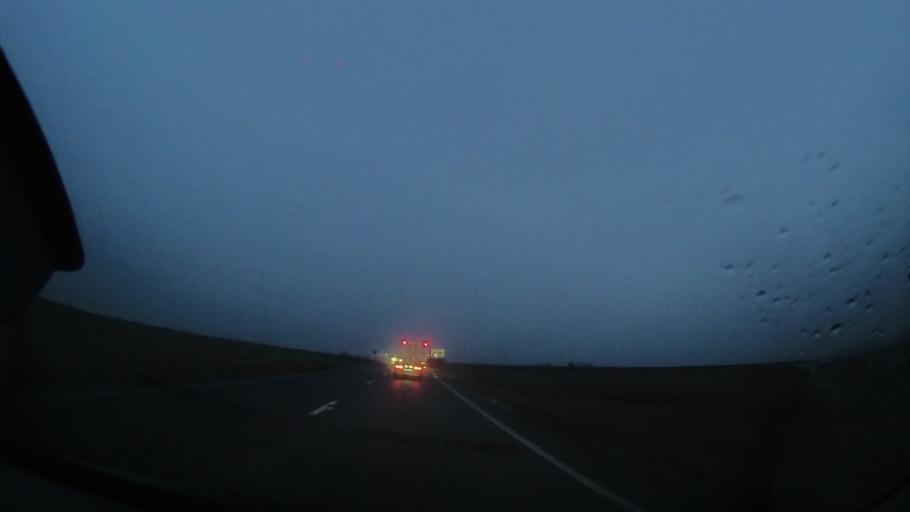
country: RO
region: Harghita
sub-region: Comuna Ditrau
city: Ditrau
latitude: 46.8297
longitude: 25.4923
